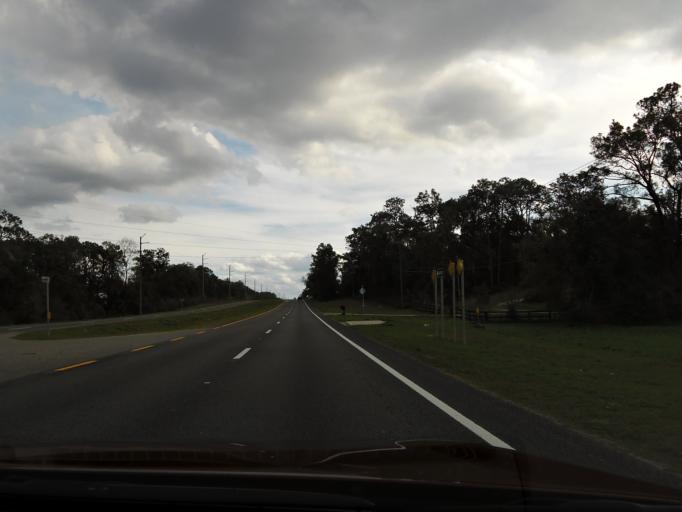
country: US
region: Florida
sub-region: Volusia County
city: De Leon Springs
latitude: 29.1014
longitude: -81.3386
